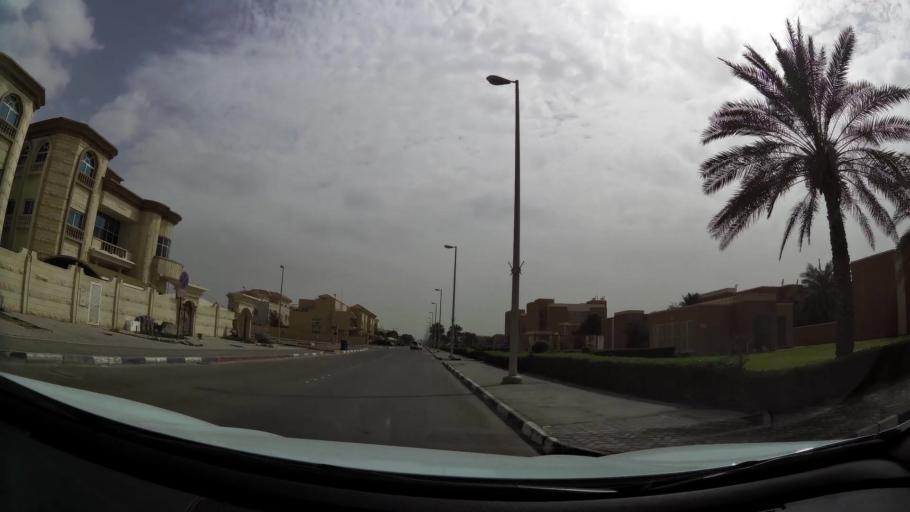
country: AE
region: Abu Dhabi
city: Abu Dhabi
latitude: 24.3944
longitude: 54.4918
